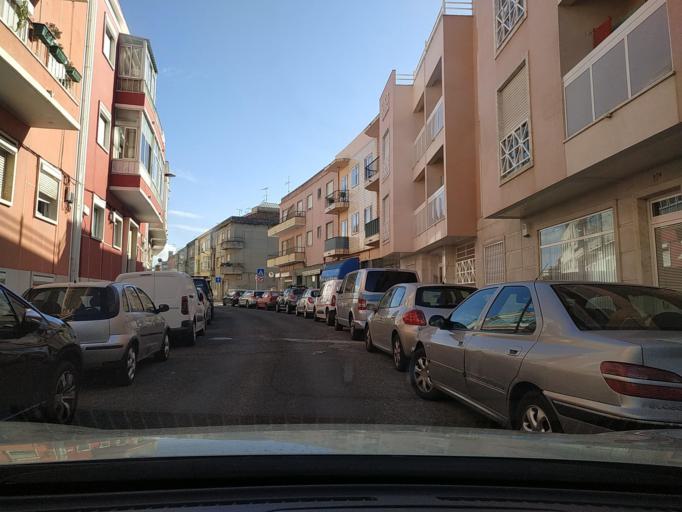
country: PT
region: Lisbon
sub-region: Amadora
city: Amadora
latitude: 38.7602
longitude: -9.2328
